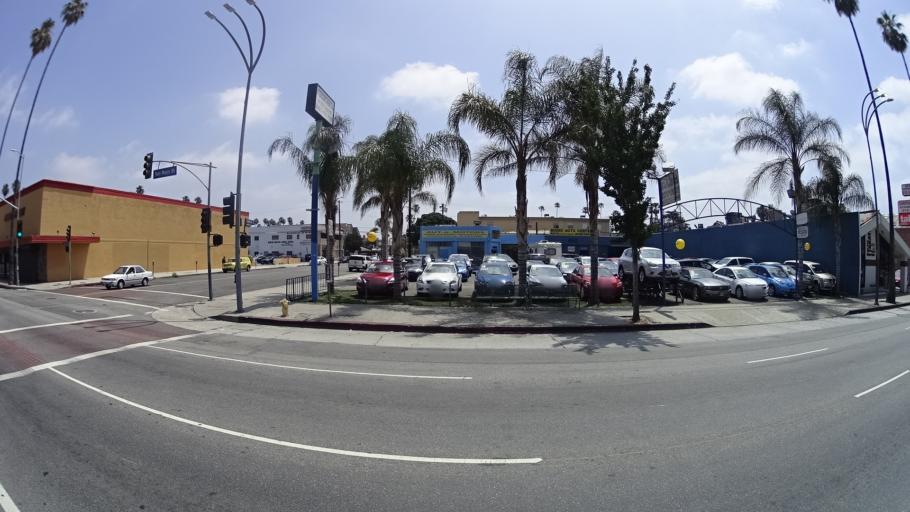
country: US
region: California
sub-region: Los Angeles County
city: Van Nuys
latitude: 34.1884
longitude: -118.4487
